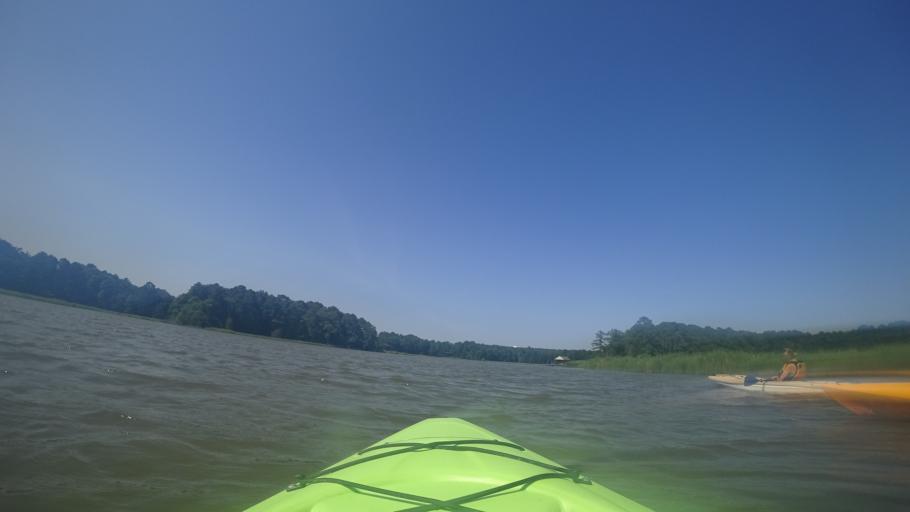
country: US
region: Virginia
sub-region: Isle of Wight County
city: Smithfield
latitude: 36.9558
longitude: -76.6166
